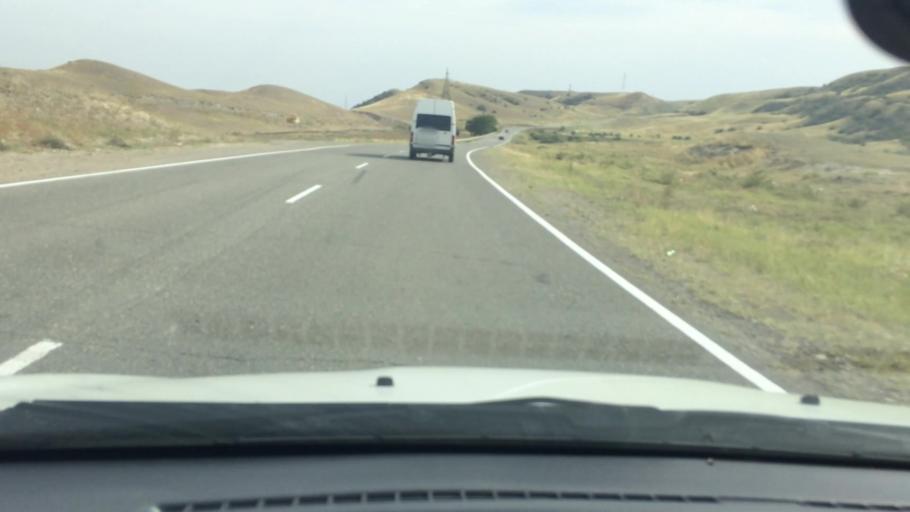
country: GE
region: Kvemo Kartli
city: Rust'avi
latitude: 41.5318
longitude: 44.9839
